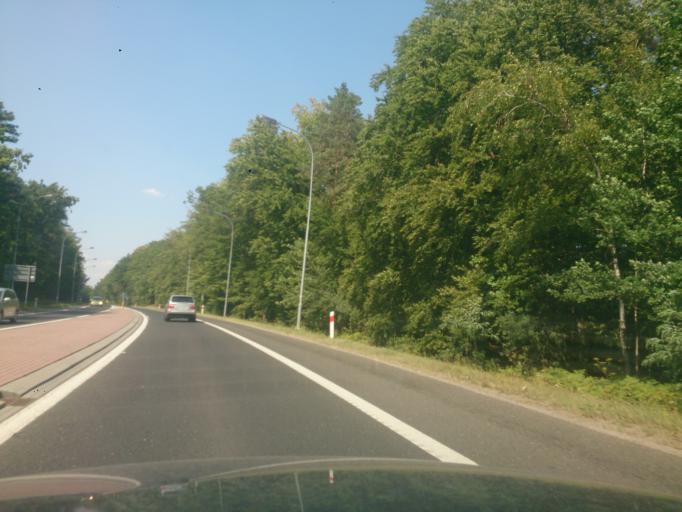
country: PL
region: Subcarpathian Voivodeship
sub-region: Powiat rzeszowski
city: Glogow Malopolski
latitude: 50.1728
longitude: 21.9384
